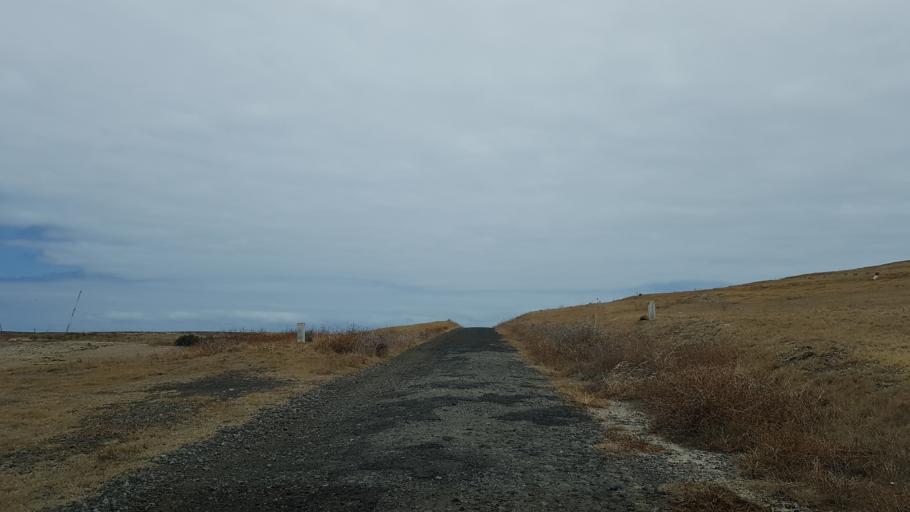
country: PT
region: Madeira
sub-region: Porto Santo
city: Camacha
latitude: 33.0903
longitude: -16.3363
